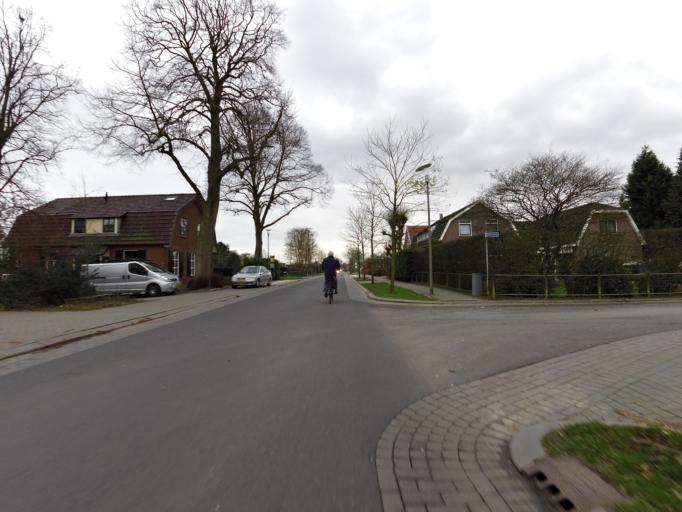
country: NL
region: Gelderland
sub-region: Gemeente Montferland
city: s-Heerenberg
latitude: 51.9094
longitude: 6.2560
